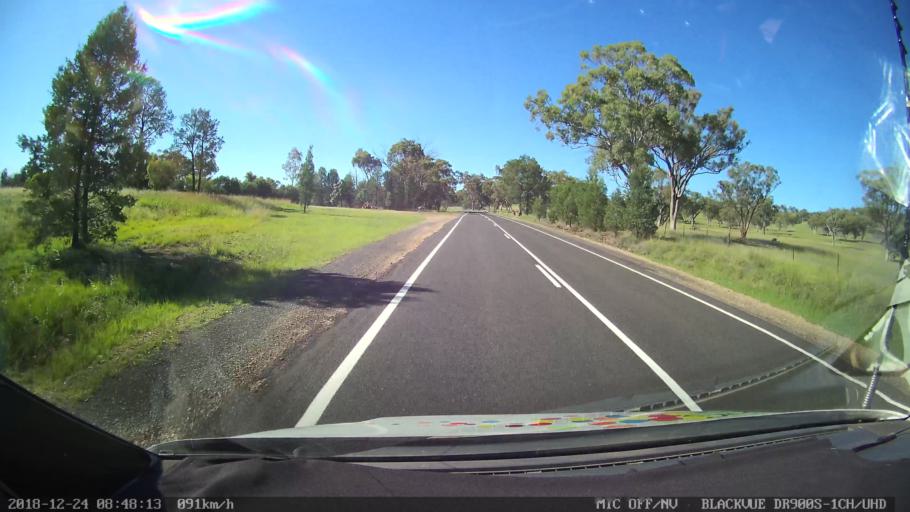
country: AU
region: New South Wales
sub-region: Liverpool Plains
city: Quirindi
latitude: -31.4526
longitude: 150.6459
